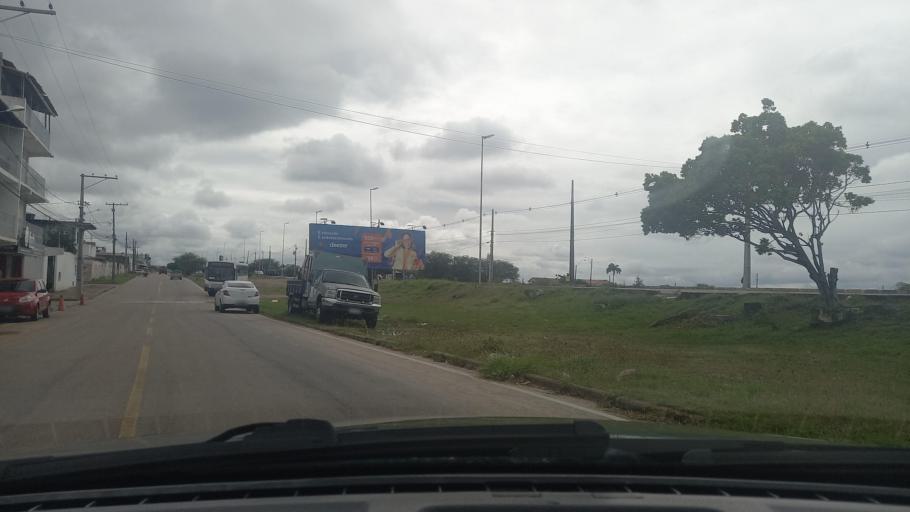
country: BR
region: Bahia
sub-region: Paulo Afonso
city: Paulo Afonso
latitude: -9.4004
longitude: -38.2399
